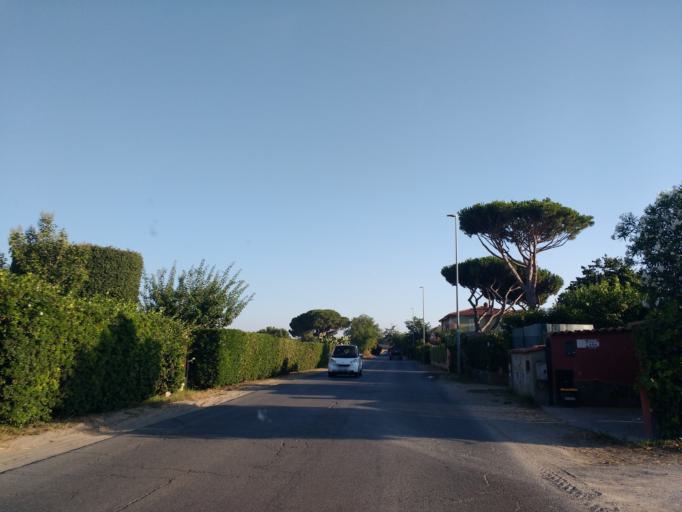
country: IT
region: Latium
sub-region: Citta metropolitana di Roma Capitale
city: Fregene
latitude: 41.8523
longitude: 12.2183
